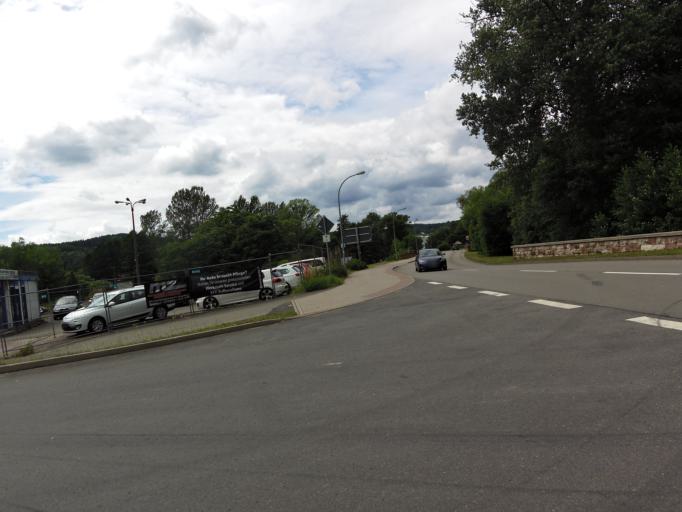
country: DE
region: Thuringia
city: Wernshausen
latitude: 50.7194
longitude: 10.3623
